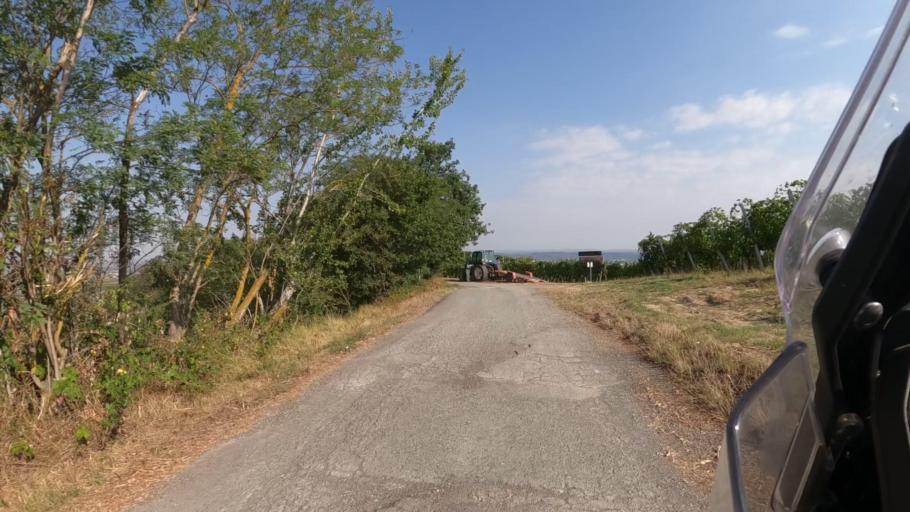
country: IT
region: Piedmont
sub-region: Provincia di Asti
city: Castel Boglione
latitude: 44.7488
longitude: 8.3872
